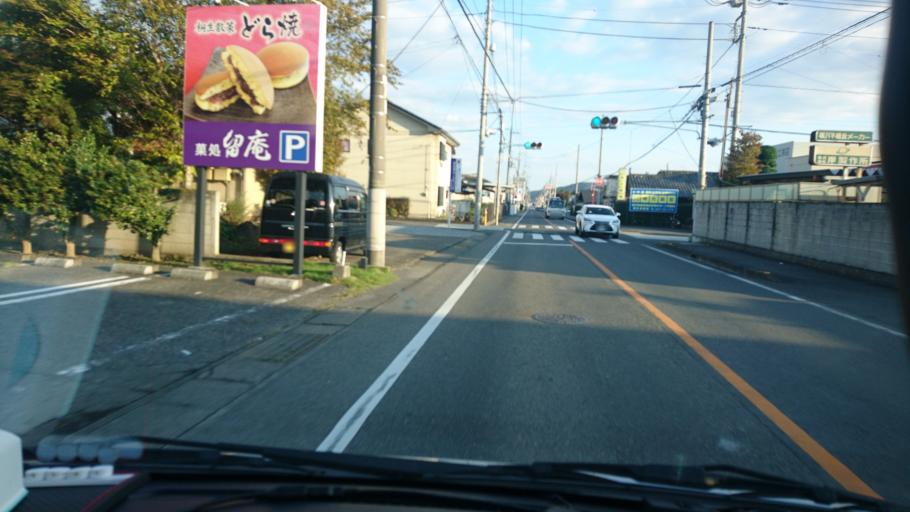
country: JP
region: Gunma
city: Kiryu
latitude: 36.3922
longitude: 139.3289
